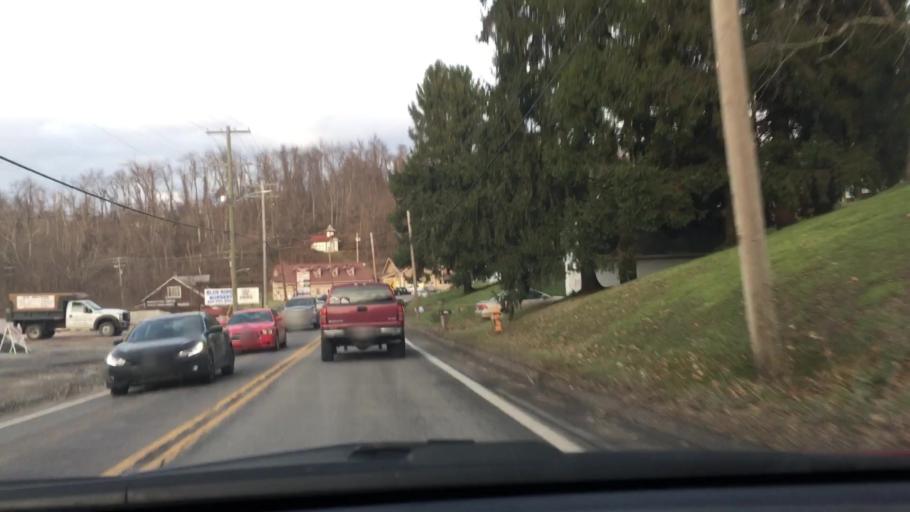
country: US
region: Pennsylvania
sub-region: Allegheny County
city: Versailles
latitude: 40.2796
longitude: -79.8363
